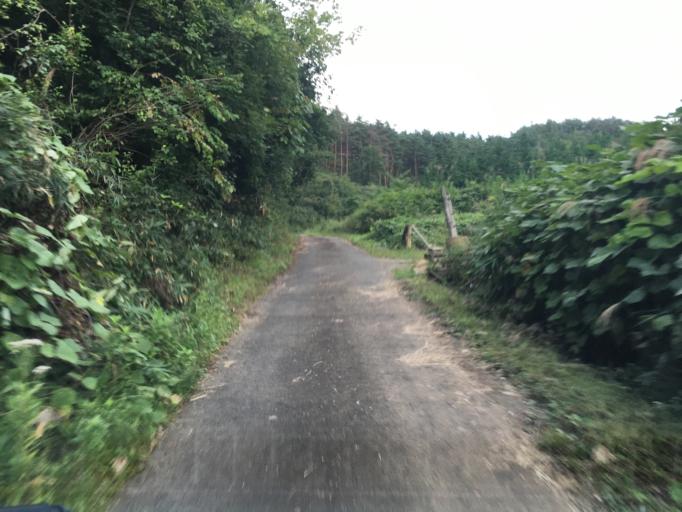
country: JP
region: Fukushima
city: Fukushima-shi
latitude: 37.7565
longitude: 140.5034
